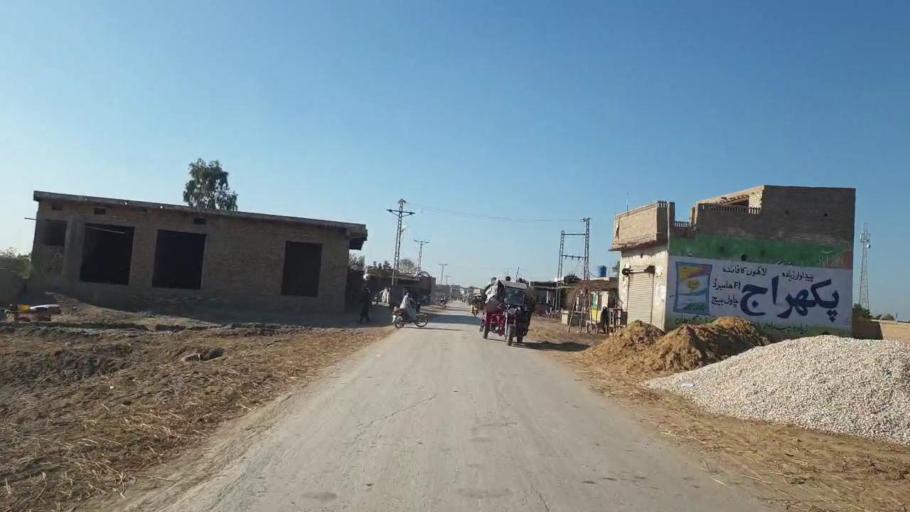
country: PK
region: Sindh
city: New Badah
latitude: 27.3253
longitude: 68.0316
